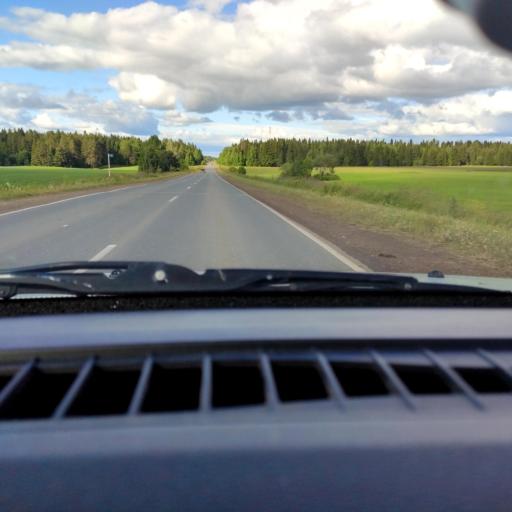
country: RU
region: Perm
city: Kungur
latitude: 57.3933
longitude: 56.8713
